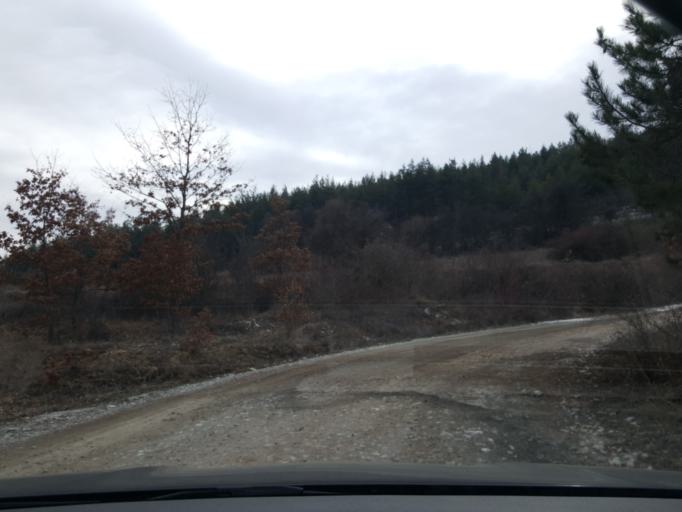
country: RS
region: Central Serbia
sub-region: Pirotski Okrug
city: Dimitrovgrad
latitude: 43.0005
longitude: 22.7508
